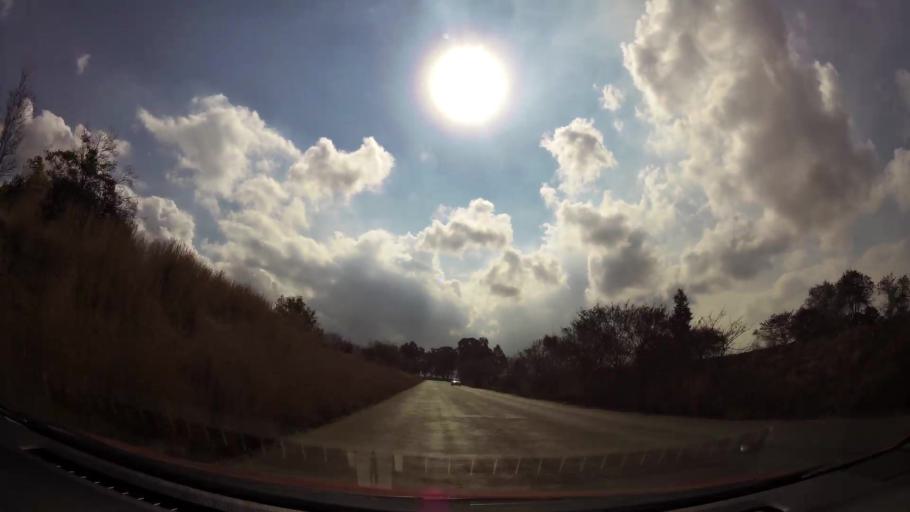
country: ZA
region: Gauteng
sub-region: Sedibeng District Municipality
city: Vanderbijlpark
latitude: -26.7432
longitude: 27.8237
